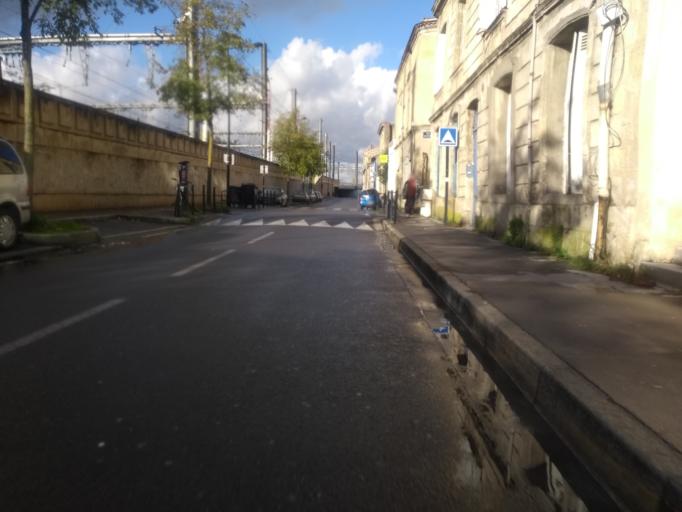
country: FR
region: Aquitaine
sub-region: Departement de la Gironde
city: Begles
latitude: 44.8273
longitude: -0.5545
